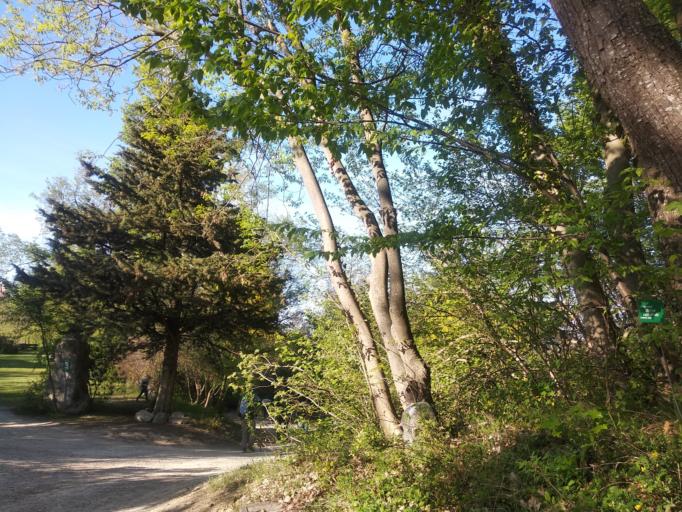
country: IT
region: Emilia-Romagna
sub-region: Provincia di Ravenna
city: Fognano
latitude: 44.2263
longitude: 11.7379
